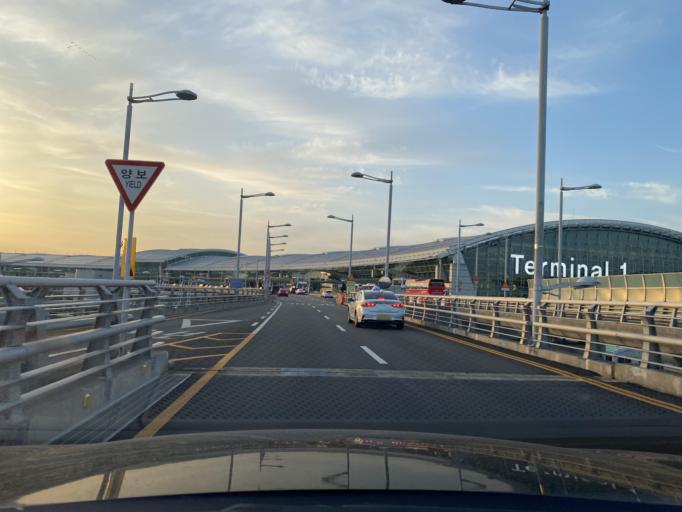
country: KR
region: Incheon
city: Incheon
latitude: 37.4489
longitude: 126.4557
